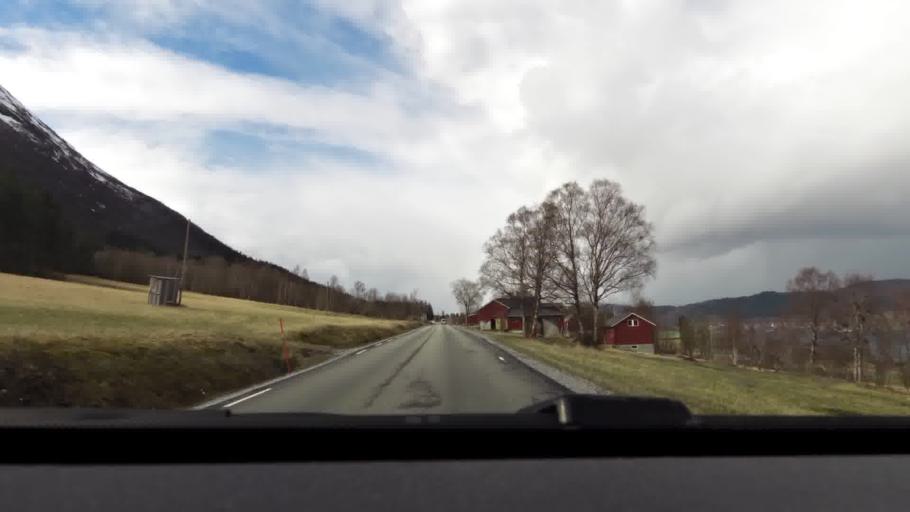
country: NO
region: More og Romsdal
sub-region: Averoy
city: Bruhagen
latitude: 63.1072
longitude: 7.6309
